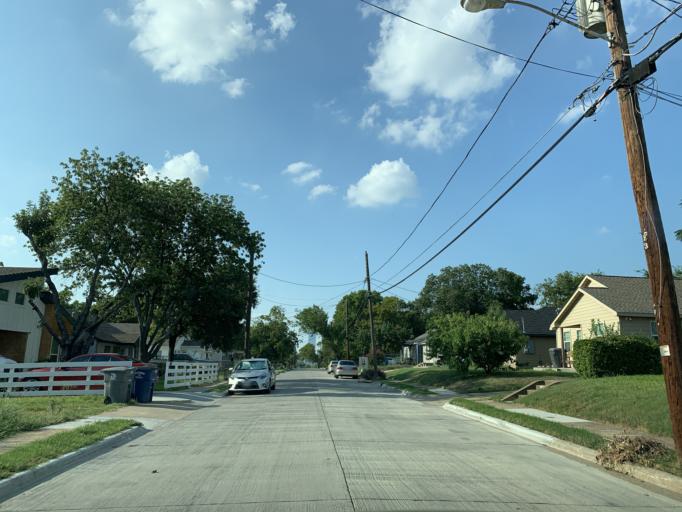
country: US
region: Texas
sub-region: Dallas County
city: Dallas
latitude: 32.7436
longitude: -96.7934
